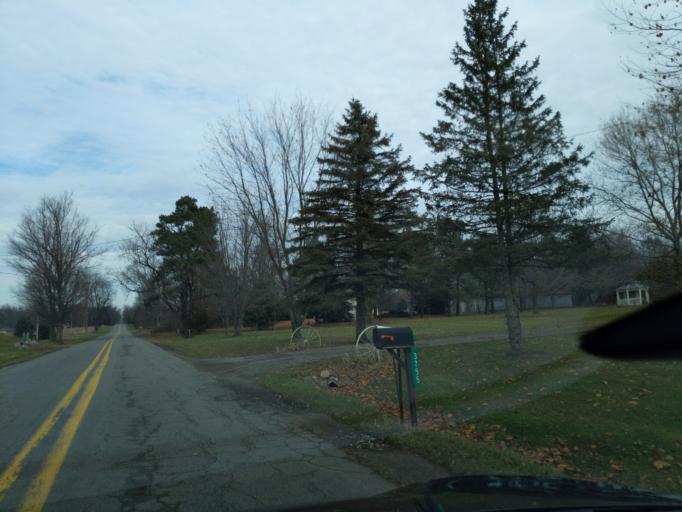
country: US
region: Michigan
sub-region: Ingham County
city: Leslie
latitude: 42.4711
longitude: -84.5020
